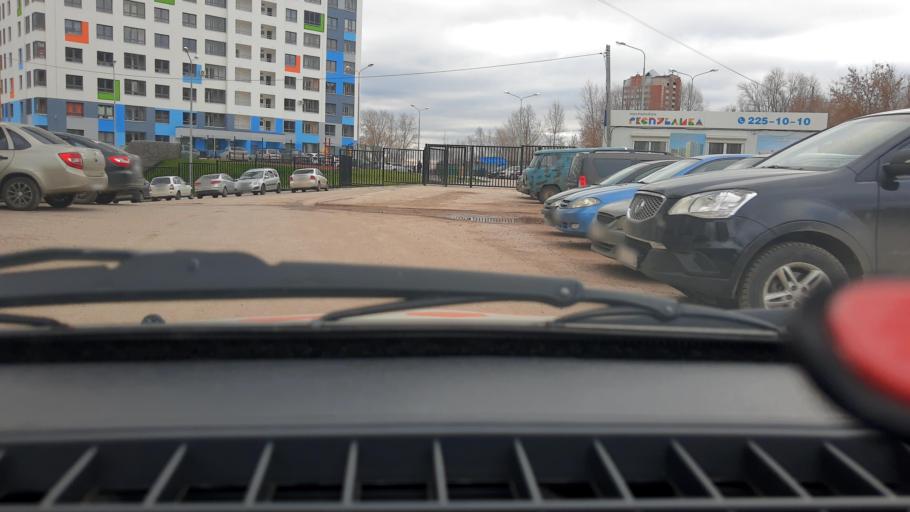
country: RU
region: Bashkortostan
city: Ufa
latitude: 54.7814
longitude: 56.0457
